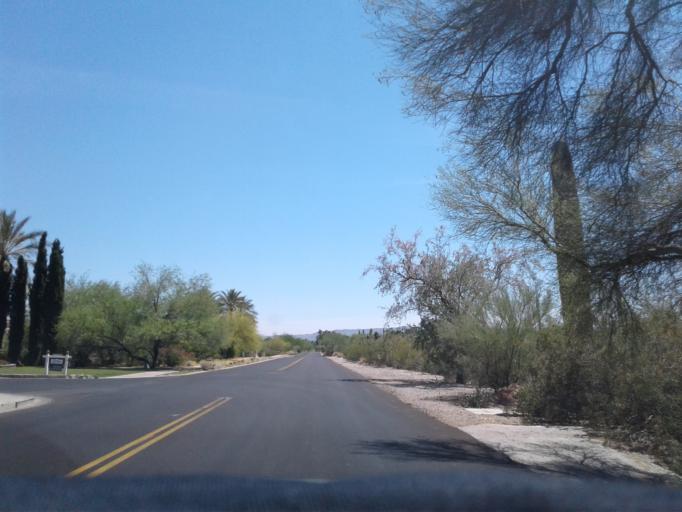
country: US
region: Arizona
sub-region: Maricopa County
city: Paradise Valley
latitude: 33.5248
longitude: -112.0040
